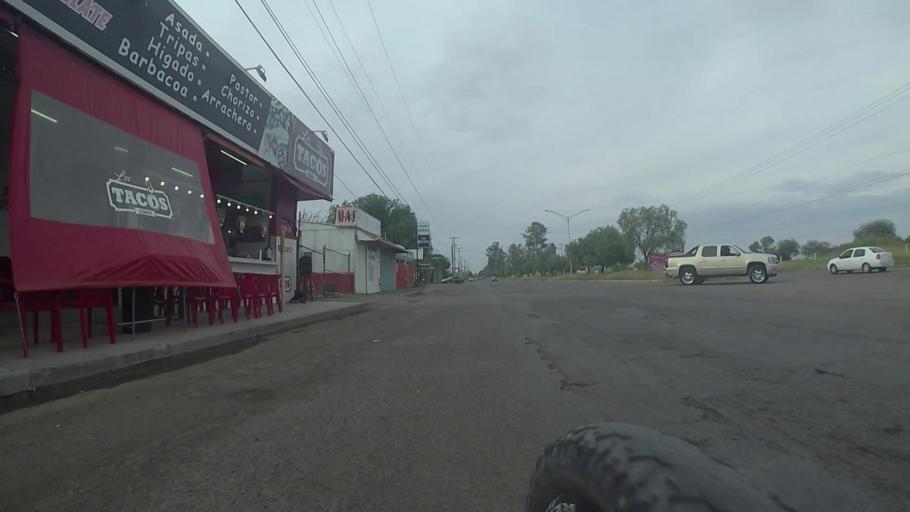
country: MX
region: Aguascalientes
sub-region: Aguascalientes
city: San Sebastian [Fraccionamiento]
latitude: 21.8353
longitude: -102.2936
